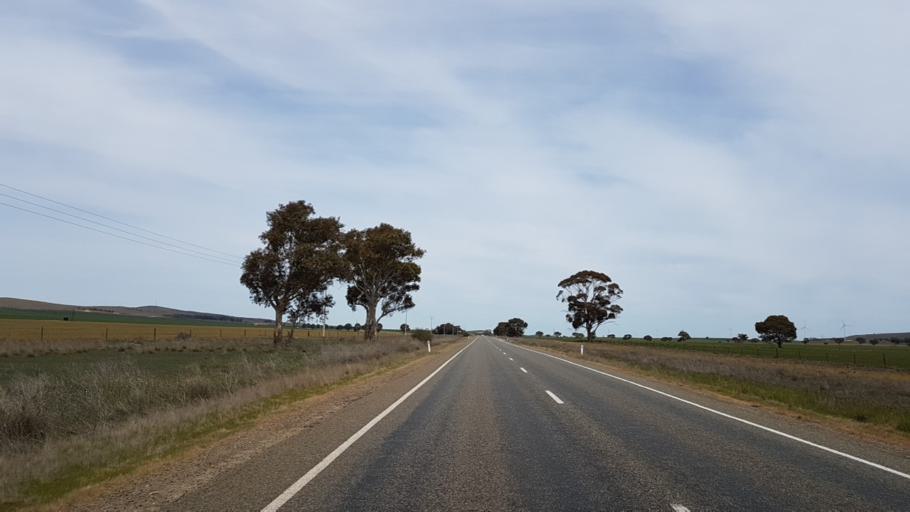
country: AU
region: South Australia
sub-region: Northern Areas
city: Jamestown
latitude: -33.0690
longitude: 138.6162
